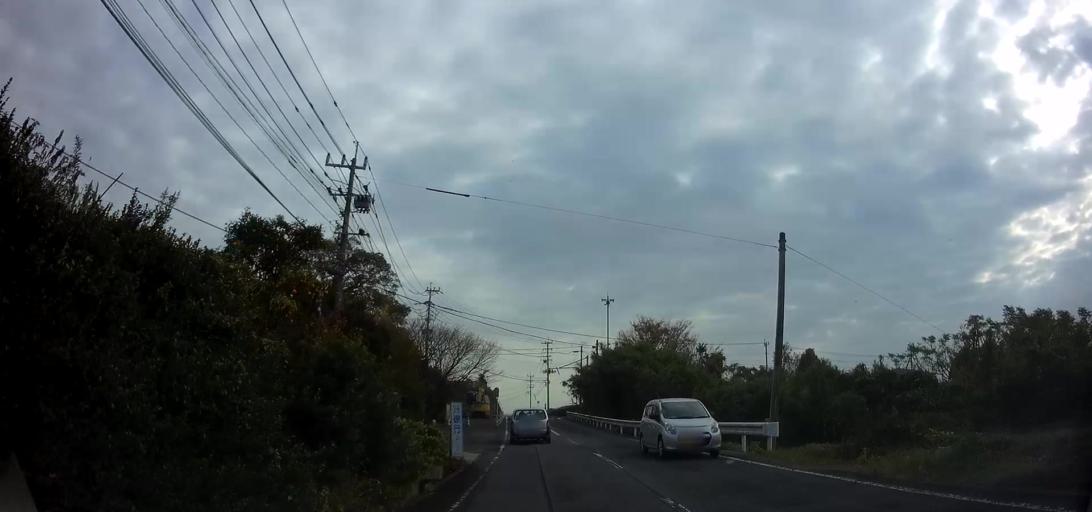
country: JP
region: Nagasaki
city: Shimabara
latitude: 32.6850
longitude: 130.2814
